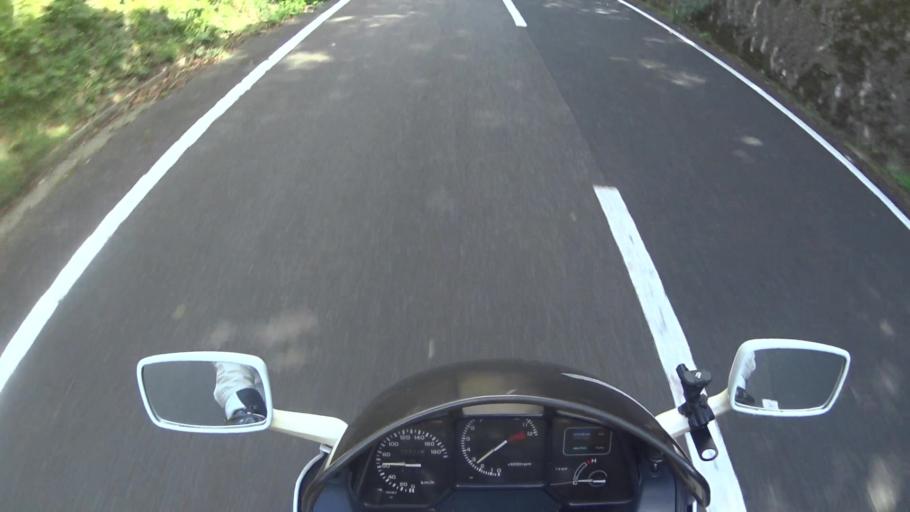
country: JP
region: Kyoto
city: Miyazu
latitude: 35.7475
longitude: 135.1703
